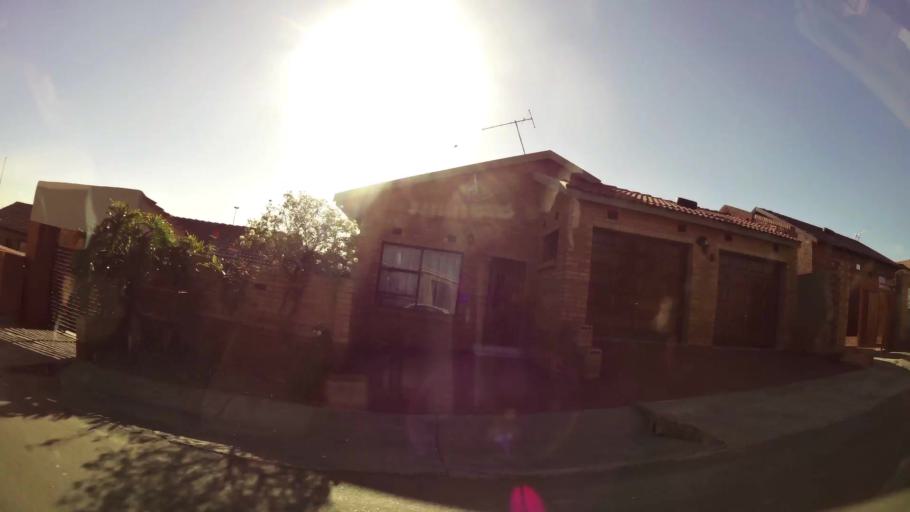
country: ZA
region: Gauteng
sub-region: Ekurhuleni Metropolitan Municipality
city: Tembisa
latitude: -26.0323
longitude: 28.2173
